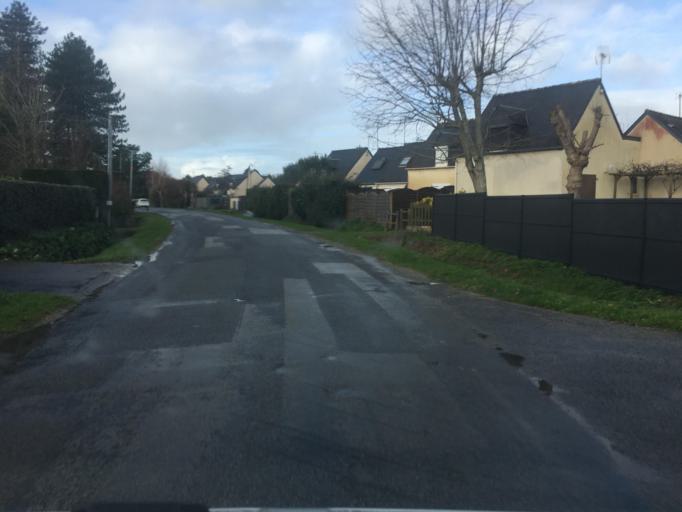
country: FR
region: Brittany
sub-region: Departement du Morbihan
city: Sarzeau
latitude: 47.5008
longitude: -2.7679
